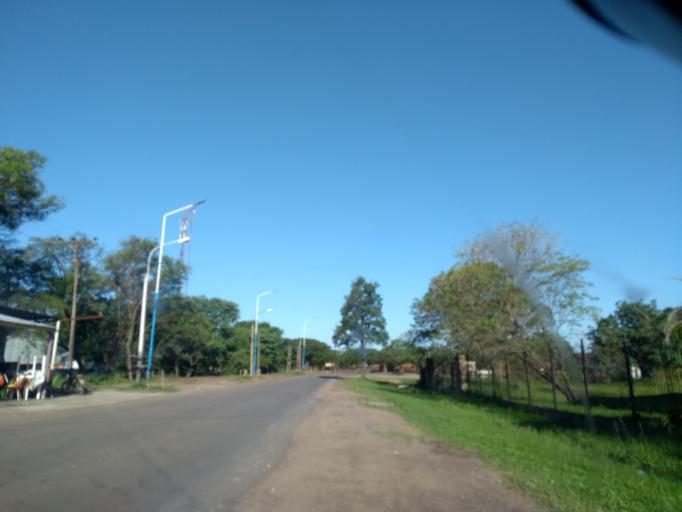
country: AR
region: Chaco
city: La Escondida
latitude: -27.1040
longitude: -59.4457
